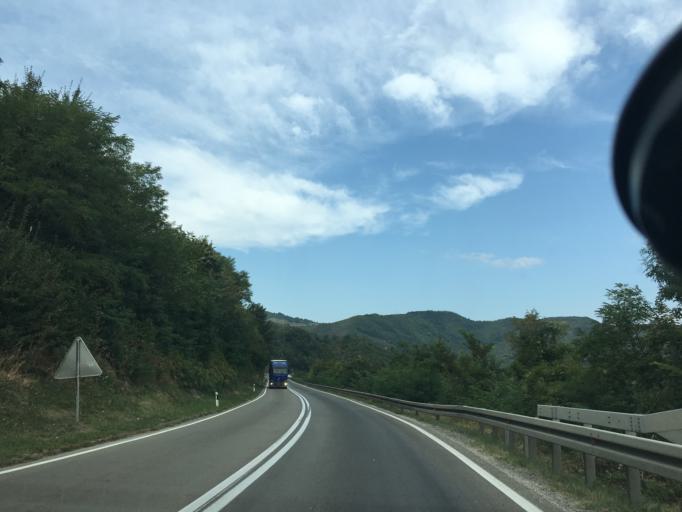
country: RS
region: Central Serbia
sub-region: Moravicki Okrug
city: Lucani
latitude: 43.9137
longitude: 20.2343
